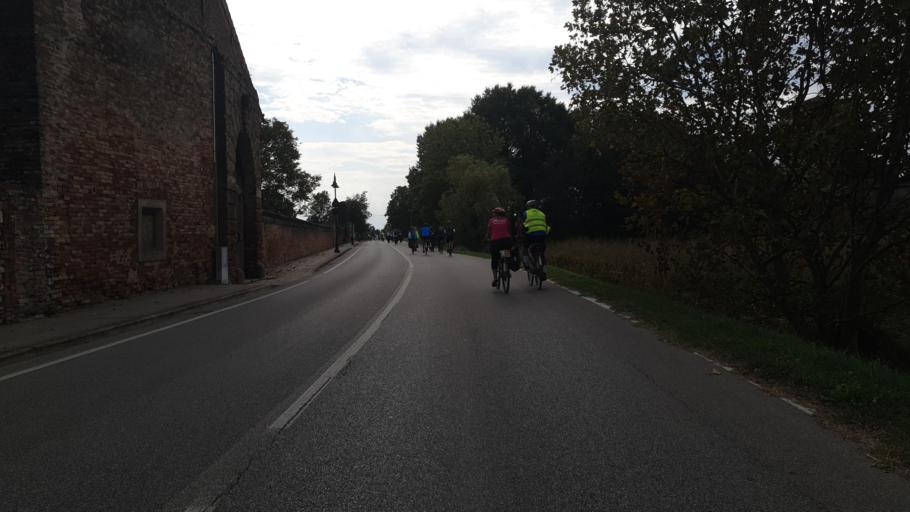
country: IT
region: Veneto
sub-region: Provincia di Vicenza
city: Poiana Maggiore
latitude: 45.2865
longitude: 11.4985
